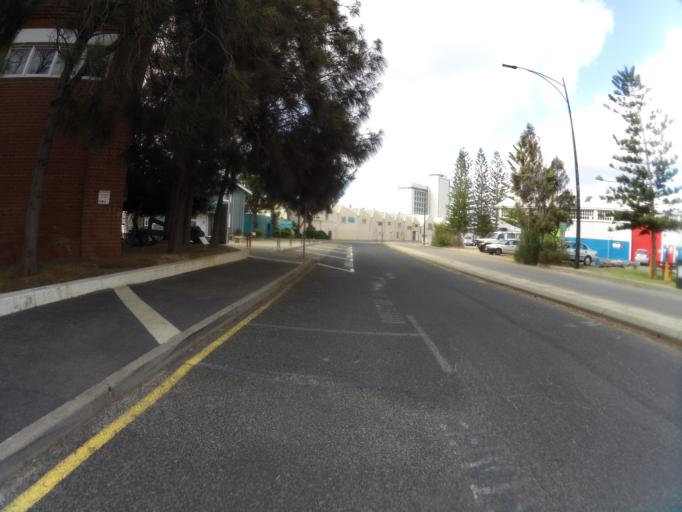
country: AU
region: Western Australia
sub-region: Fremantle
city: South Fremantle
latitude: -32.0560
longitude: 115.7401
